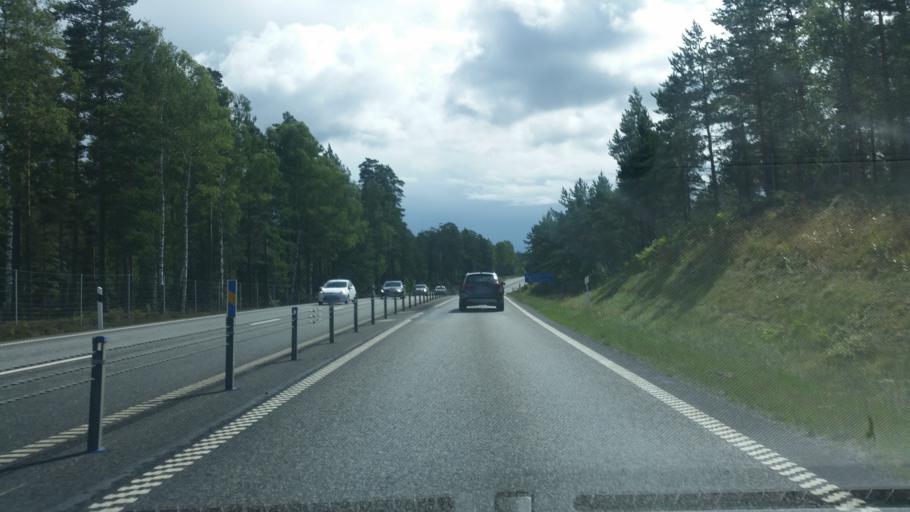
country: SE
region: Joenkoeping
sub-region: Mullsjo Kommun
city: Mullsjoe
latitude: 57.7648
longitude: 13.8261
